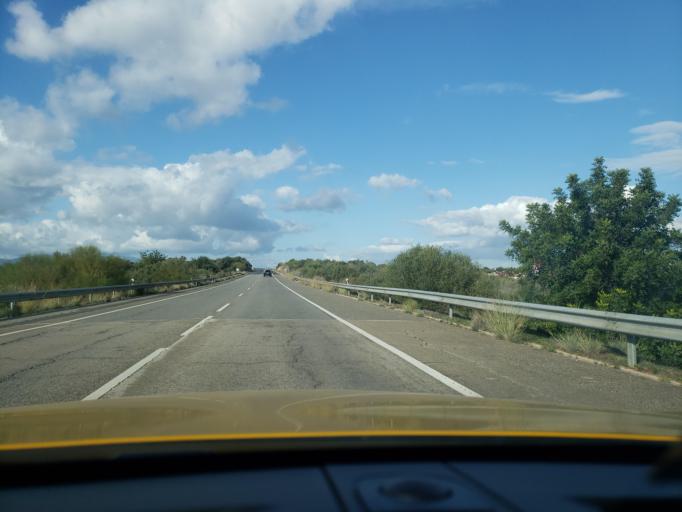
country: PT
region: Faro
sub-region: Silves
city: Silves
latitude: 37.1708
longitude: -8.4428
